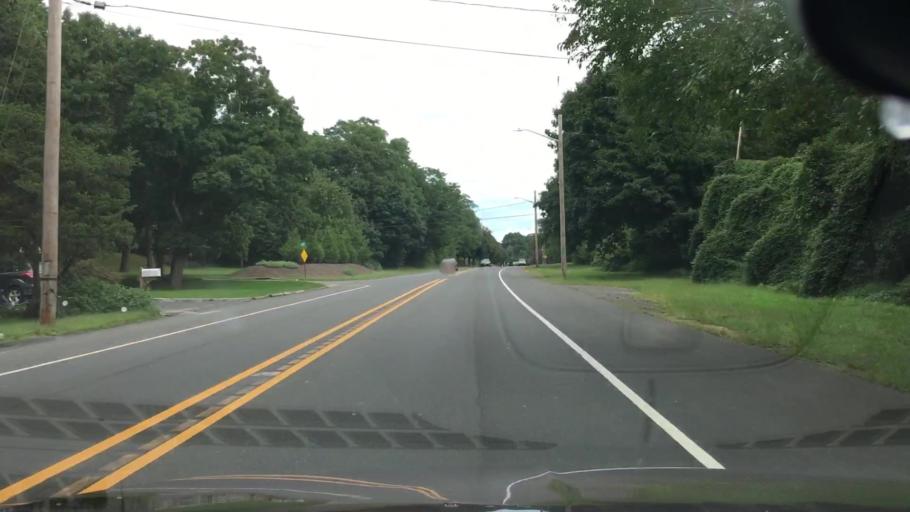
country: US
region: New York
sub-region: Suffolk County
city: Village of the Branch
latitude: 40.8686
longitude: -73.1745
